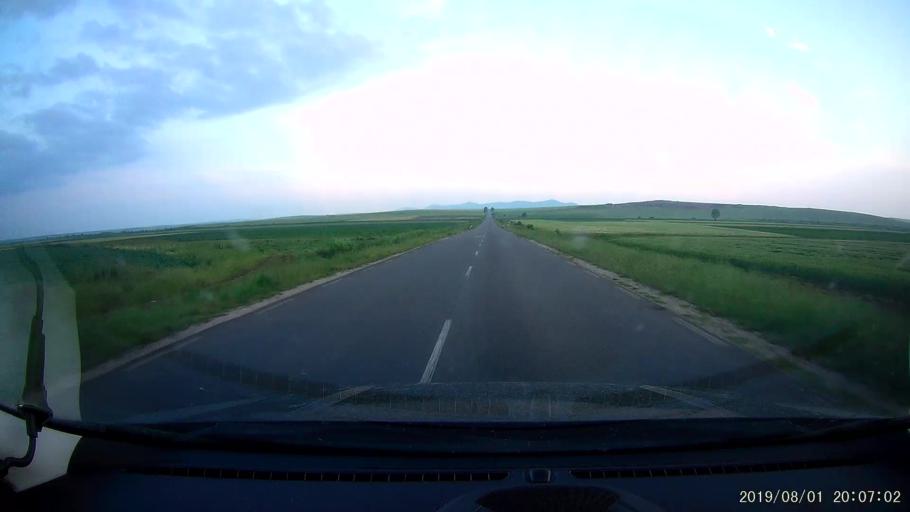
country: BG
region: Yambol
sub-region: Obshtina Yambol
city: Yambol
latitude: 42.5280
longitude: 26.5617
